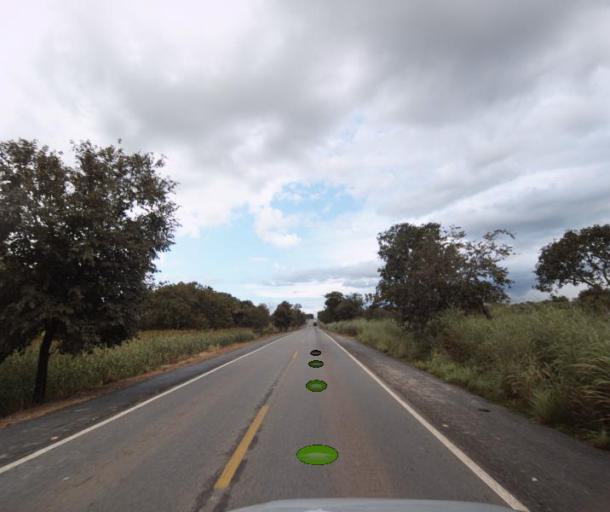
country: BR
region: Goias
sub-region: Porangatu
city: Porangatu
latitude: -13.3441
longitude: -49.1219
